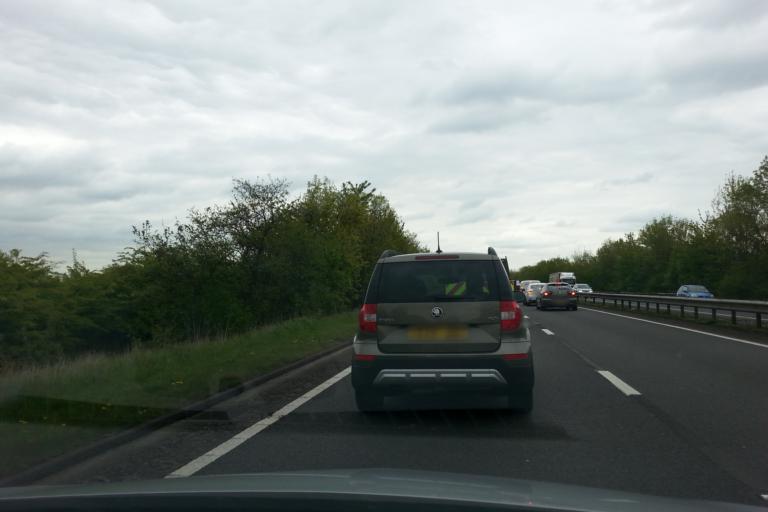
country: GB
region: England
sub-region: Leicestershire
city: Castle Donington
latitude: 52.7981
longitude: -1.3612
